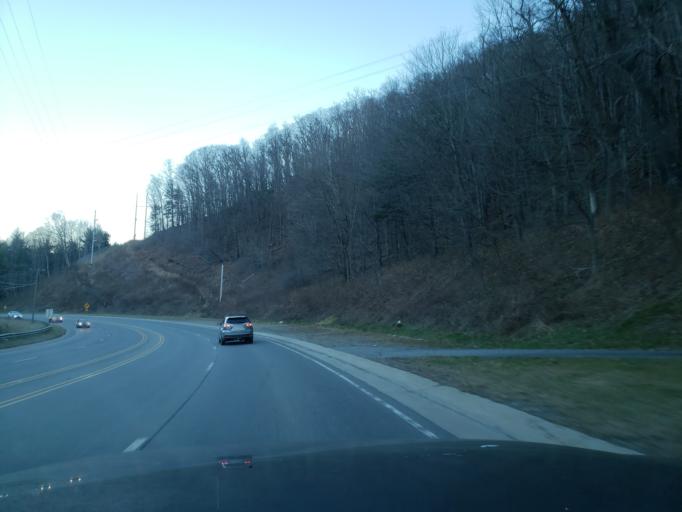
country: US
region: North Carolina
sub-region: Watauga County
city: Boone
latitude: 36.1880
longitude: -81.6529
